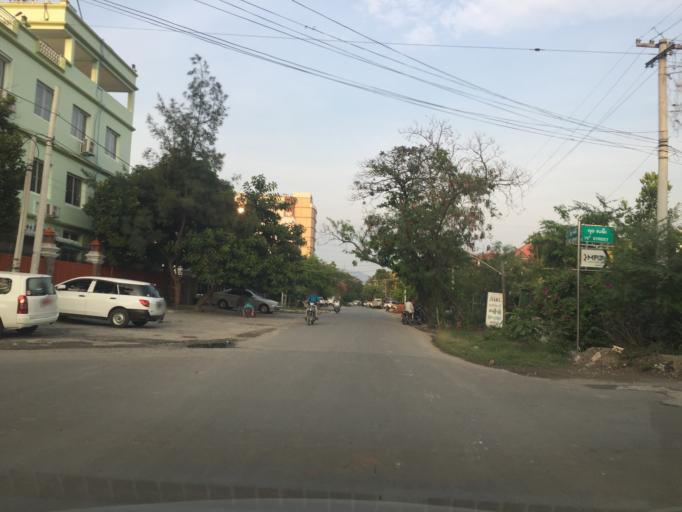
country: MM
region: Mandalay
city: Mandalay
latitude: 21.9714
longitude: 96.1000
